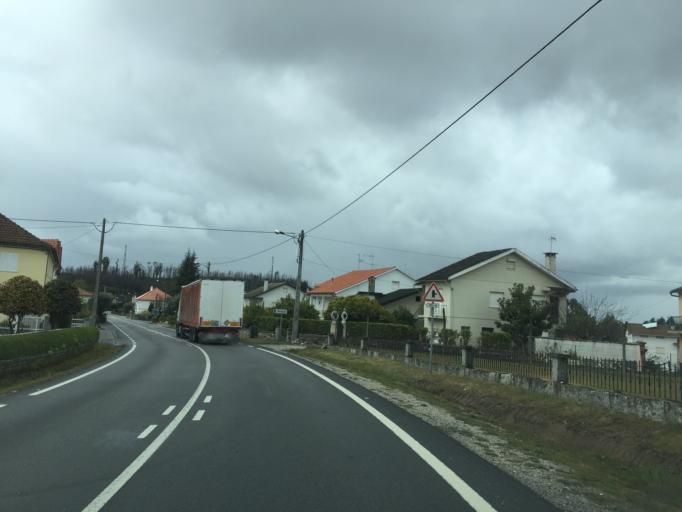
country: PT
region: Coimbra
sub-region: Oliveira do Hospital
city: Oliveira do Hospital
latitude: 40.3239
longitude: -7.9189
